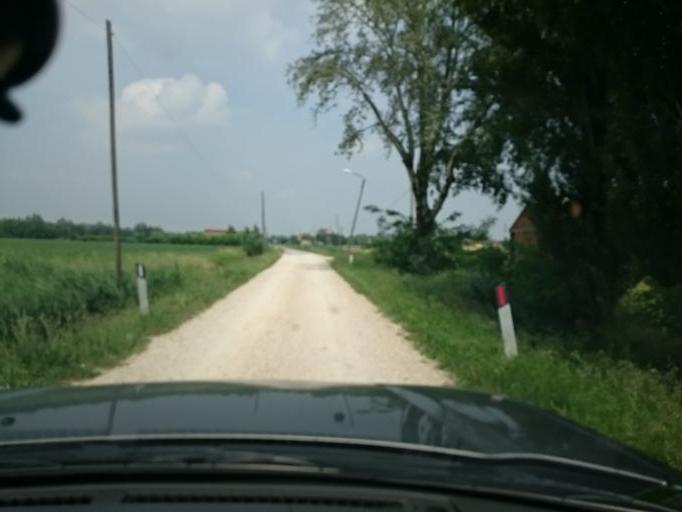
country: IT
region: Veneto
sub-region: Provincia di Padova
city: Arzergrande
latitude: 45.2599
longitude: 12.0527
